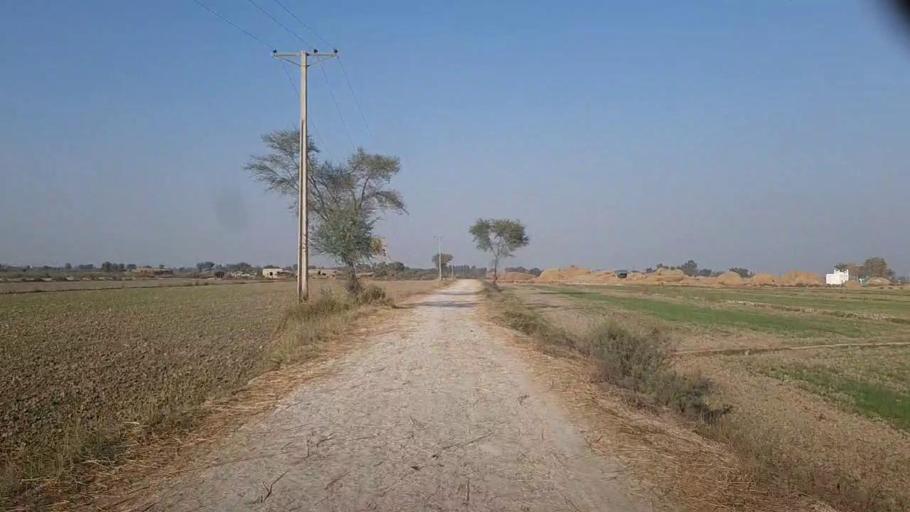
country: PK
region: Sindh
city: Thul
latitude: 28.1642
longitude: 68.8154
